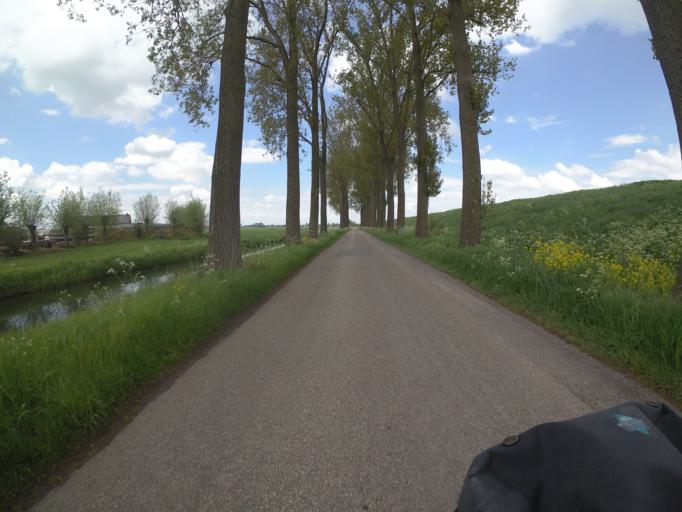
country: NL
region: North Brabant
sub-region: Gemeente Waalwijk
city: Waalwijk
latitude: 51.7212
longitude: 5.0730
